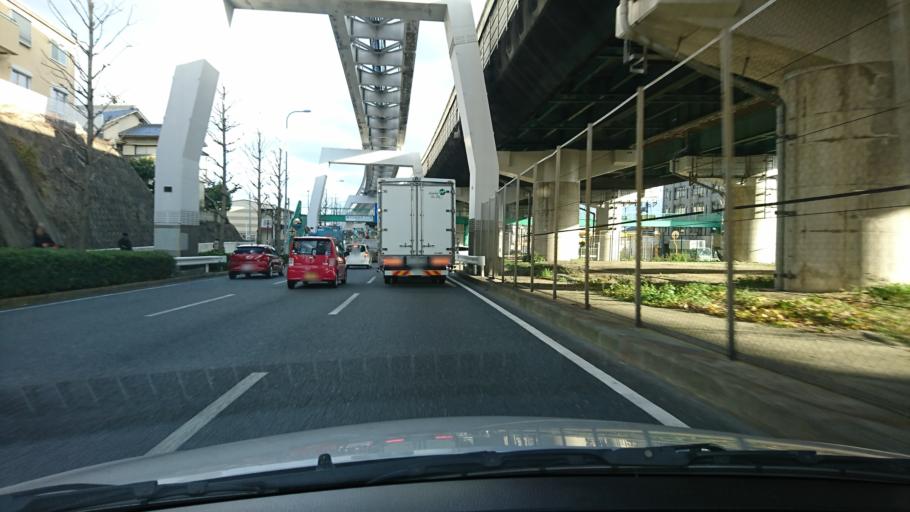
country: JP
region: Osaka
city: Toyonaka
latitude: 34.7999
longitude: 135.4602
